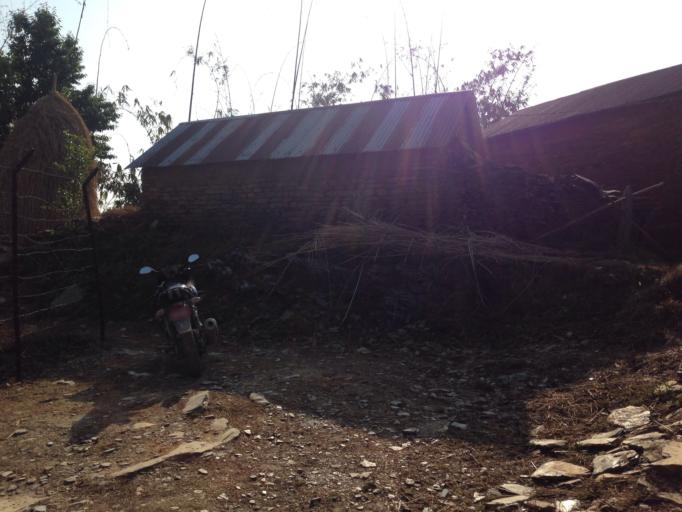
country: NP
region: Western Region
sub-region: Gandaki Zone
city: Pokhara
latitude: 28.1994
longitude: 83.9295
